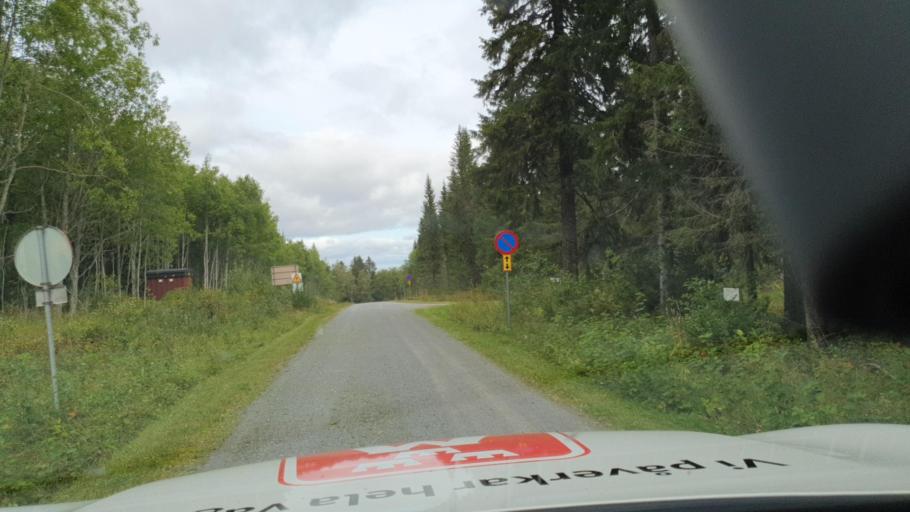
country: SE
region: Jaemtland
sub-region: OEstersunds Kommun
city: Ostersund
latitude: 63.1133
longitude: 14.6013
